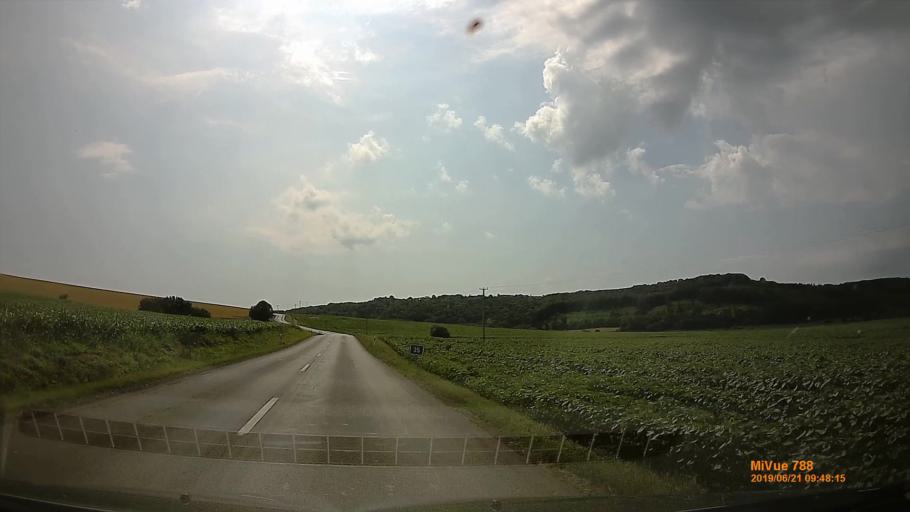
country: HU
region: Baranya
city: Sasd
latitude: 46.2683
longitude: 18.0255
